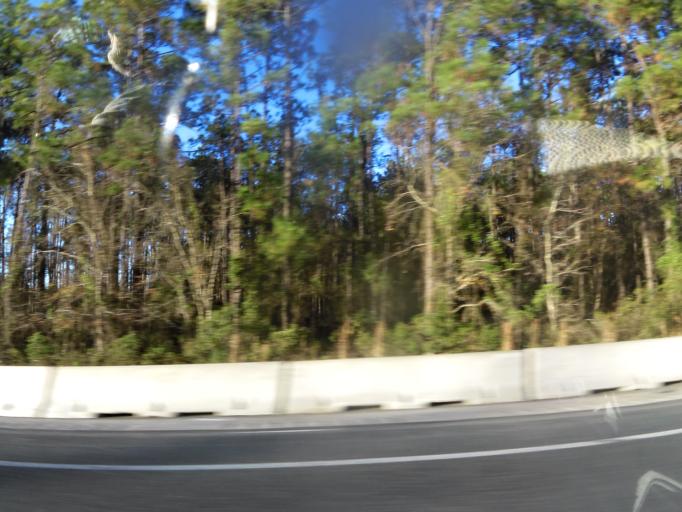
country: US
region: Florida
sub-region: Duval County
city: Baldwin
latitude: 30.2904
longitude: -81.9650
